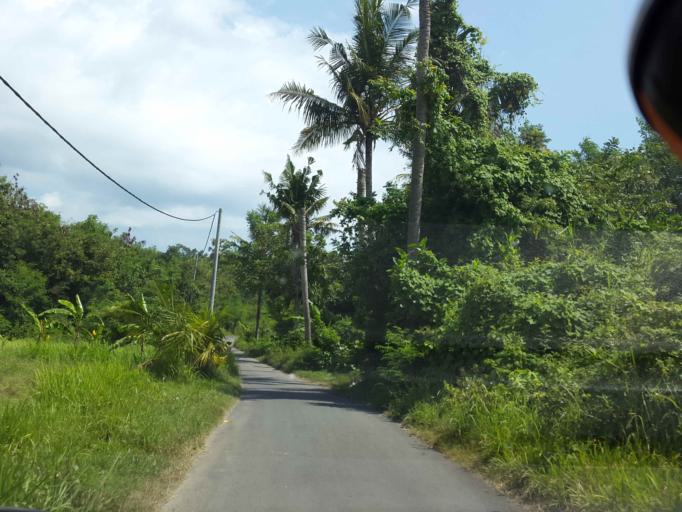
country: ID
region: Bali
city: Klungkung
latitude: -8.5632
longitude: 115.3803
